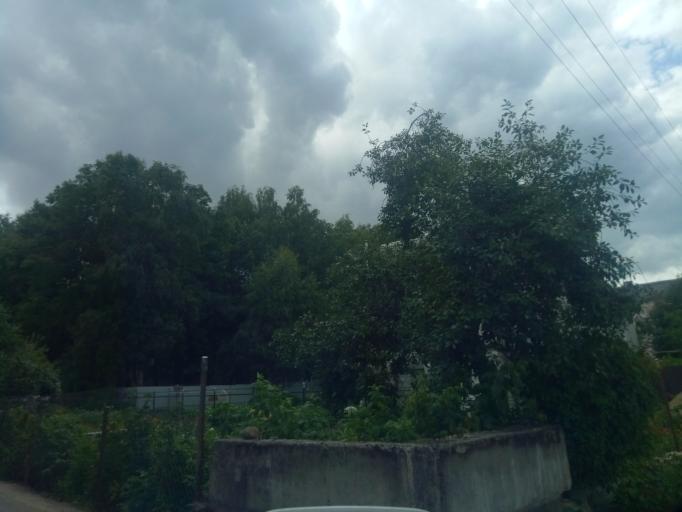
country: BY
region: Minsk
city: Zhdanovichy
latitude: 53.9382
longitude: 27.4199
